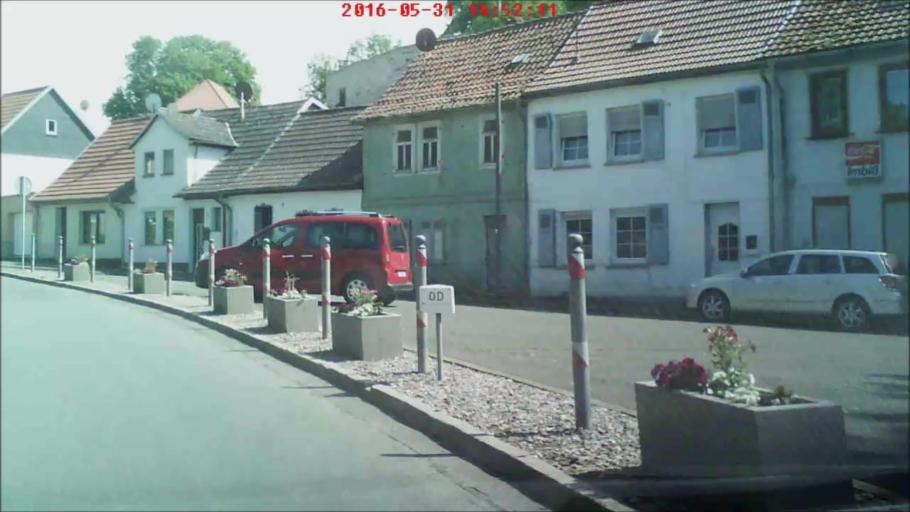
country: DE
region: Thuringia
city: Weissensee
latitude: 51.2020
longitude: 11.0624
